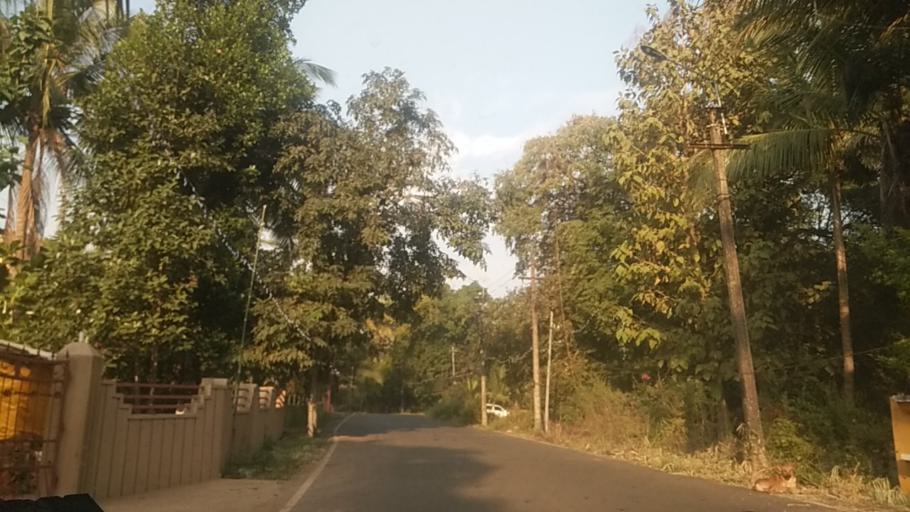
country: IN
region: Goa
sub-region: South Goa
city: Chinchinim
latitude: 15.2327
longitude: 73.9916
